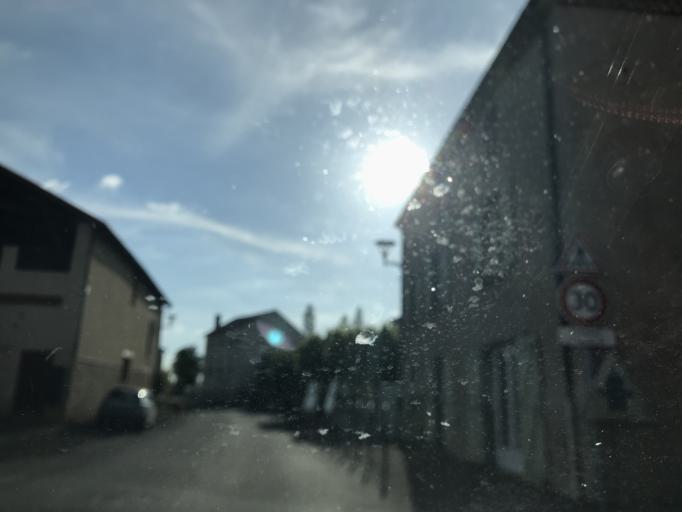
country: FR
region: Auvergne
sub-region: Departement du Puy-de-Dome
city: Courpiere
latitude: 45.7221
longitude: 3.4705
